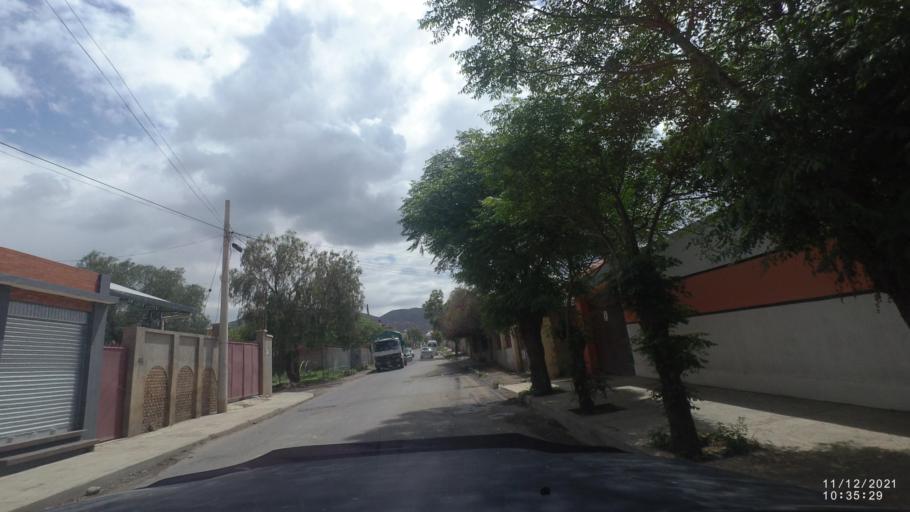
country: BO
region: Cochabamba
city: Cochabamba
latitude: -17.4512
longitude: -66.1282
